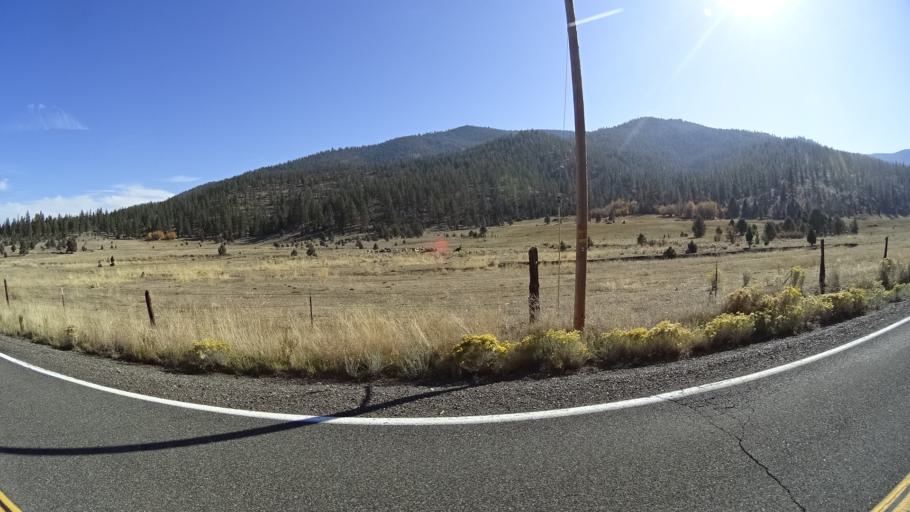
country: US
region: California
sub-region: Siskiyou County
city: Weed
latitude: 41.4773
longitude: -122.5753
